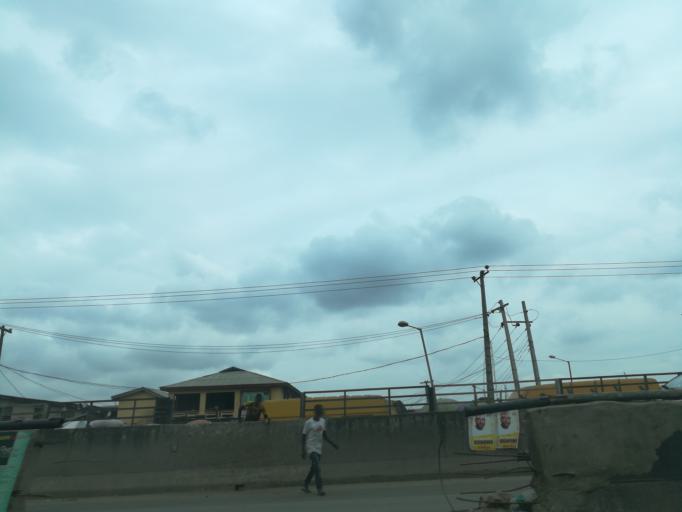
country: NG
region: Lagos
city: Ojota
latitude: 6.6067
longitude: 3.3928
